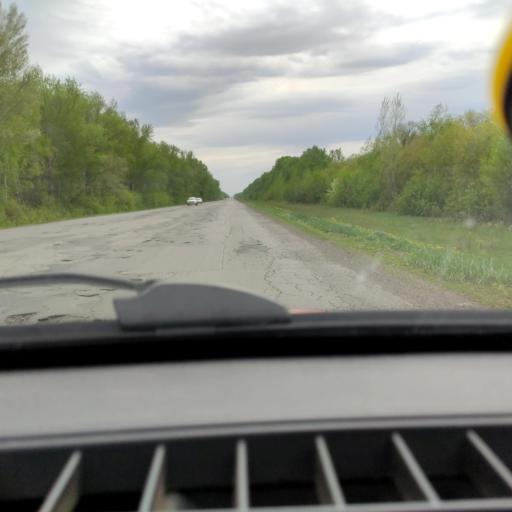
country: RU
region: Samara
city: Tol'yatti
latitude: 53.6533
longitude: 49.4236
